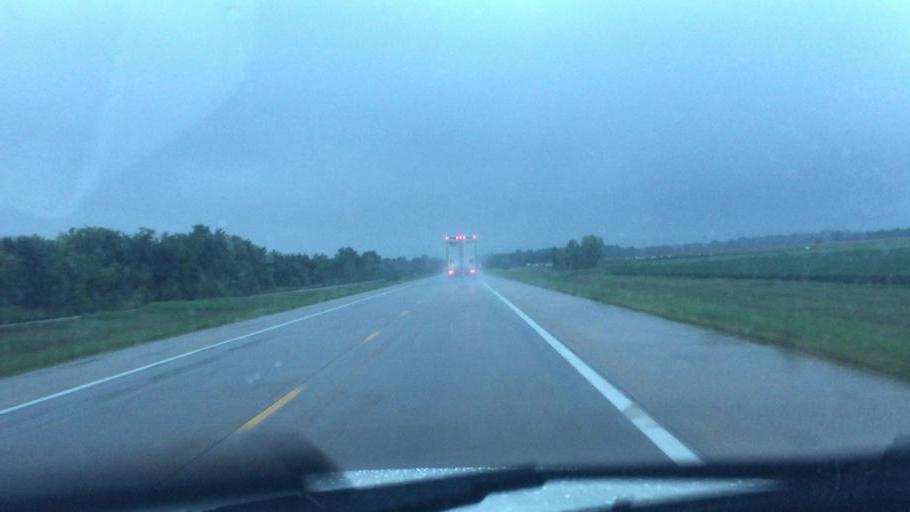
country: US
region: Kansas
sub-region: Neosho County
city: Chanute
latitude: 37.5674
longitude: -95.4710
